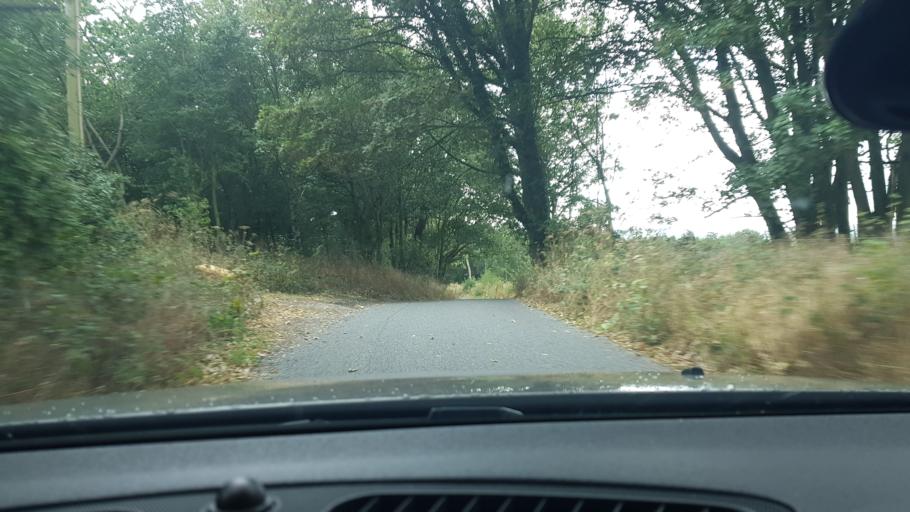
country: GB
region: England
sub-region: West Berkshire
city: Wickham
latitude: 51.4399
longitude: -1.4354
